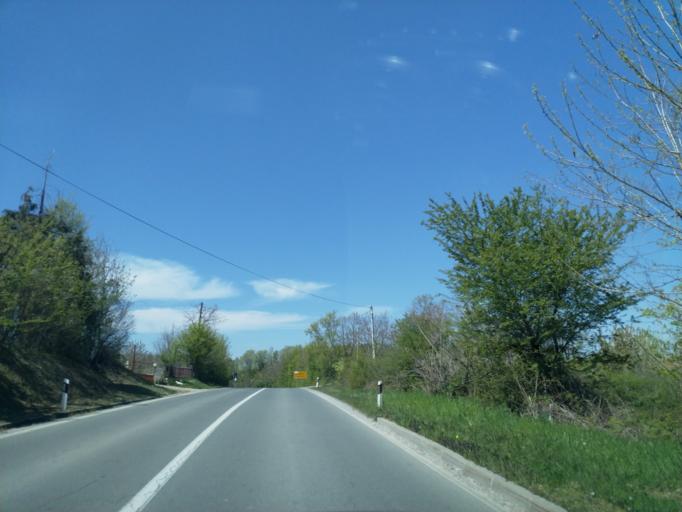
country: RS
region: Central Serbia
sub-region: Belgrade
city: Lazarevac
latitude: 44.3719
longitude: 20.3171
